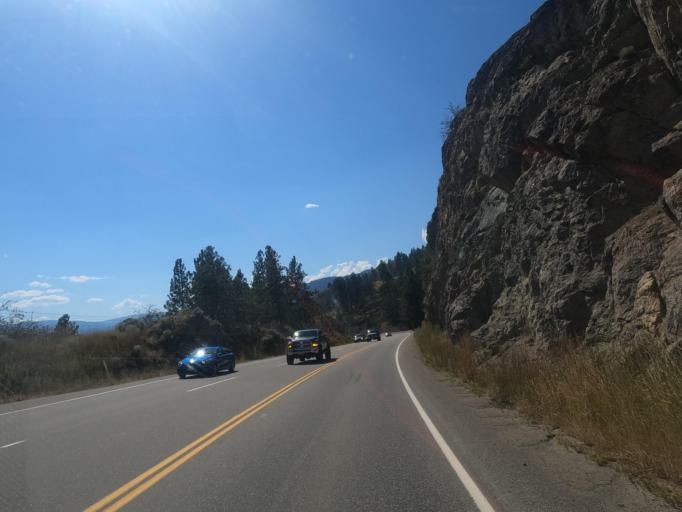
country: CA
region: British Columbia
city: Peachland
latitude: 49.8004
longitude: -119.6742
